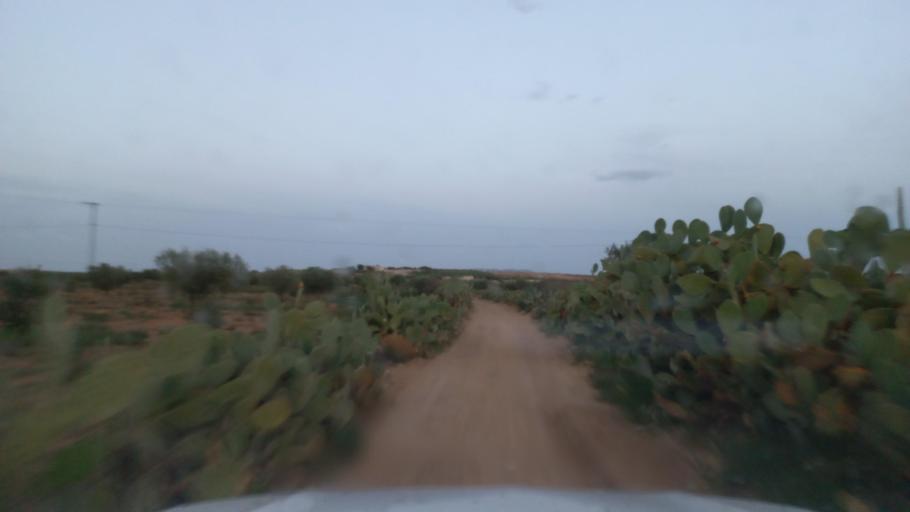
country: TN
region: Al Qasrayn
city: Sbiba
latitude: 35.3546
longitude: 9.0482
